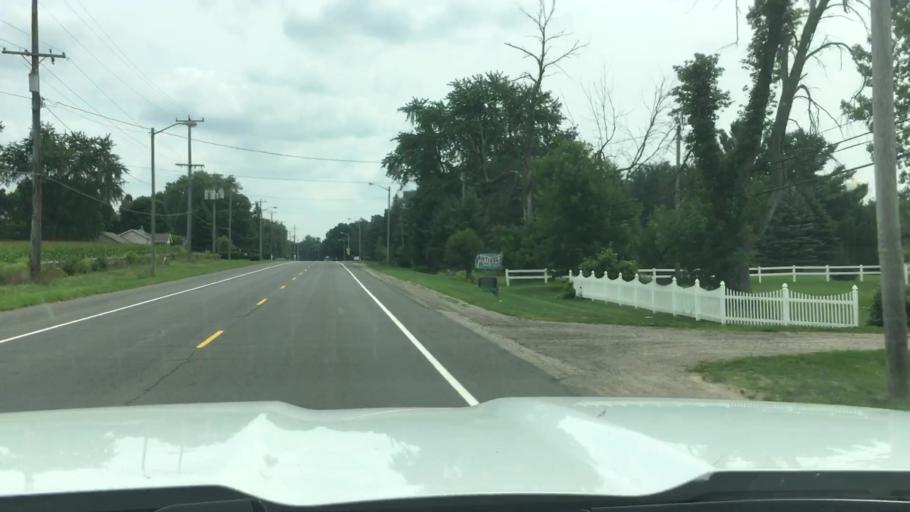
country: US
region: Michigan
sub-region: Ingham County
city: Webberville
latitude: 42.6683
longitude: -84.1934
